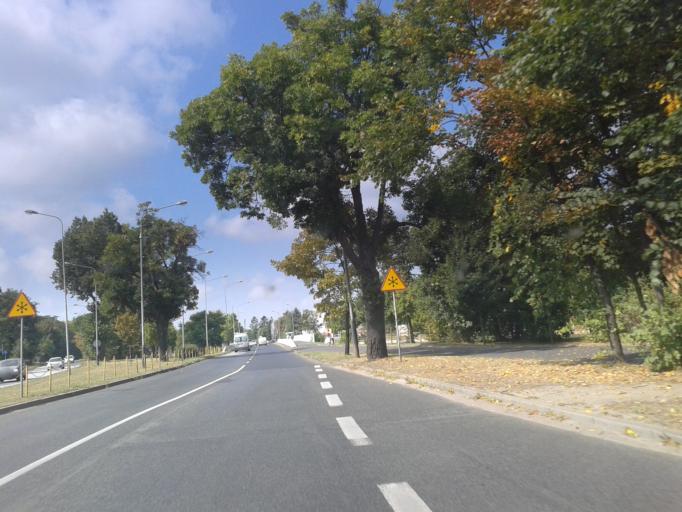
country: PL
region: Greater Poland Voivodeship
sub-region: Powiat poznanski
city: Suchy Las
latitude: 52.4298
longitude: 16.8466
